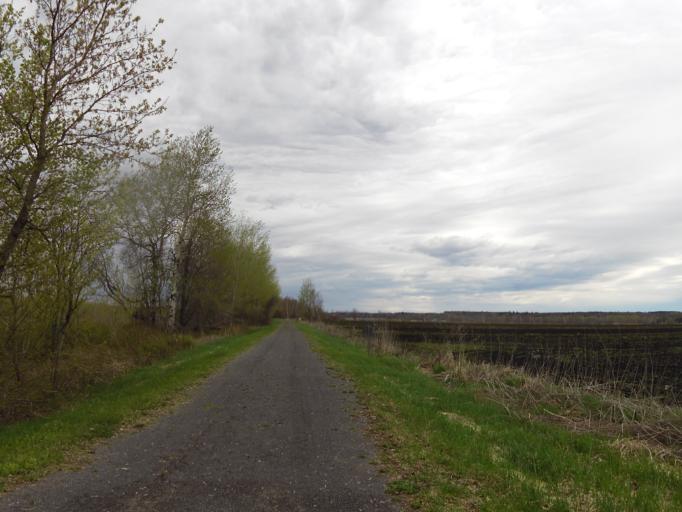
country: CA
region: Quebec
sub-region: Outaouais
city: Papineauville
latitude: 45.5401
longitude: -74.8615
